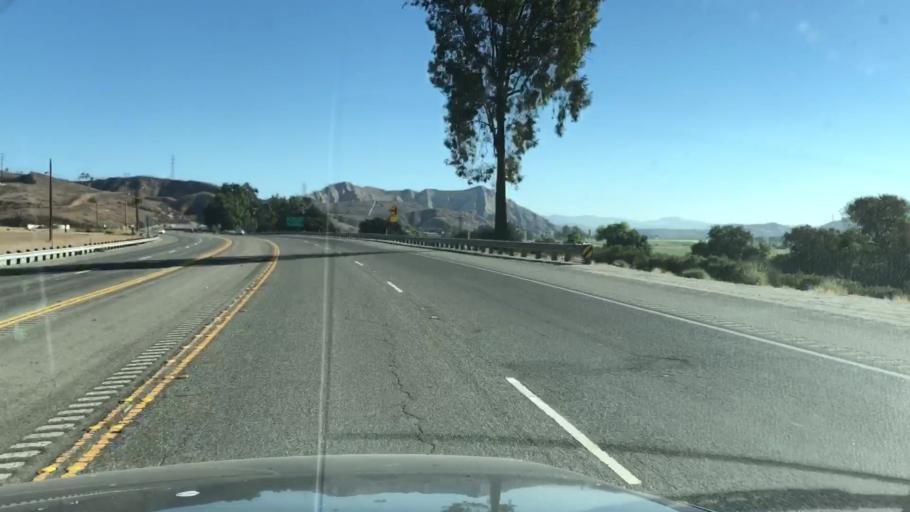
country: US
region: California
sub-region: Los Angeles County
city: Val Verde
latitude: 34.4171
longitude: -118.6593
